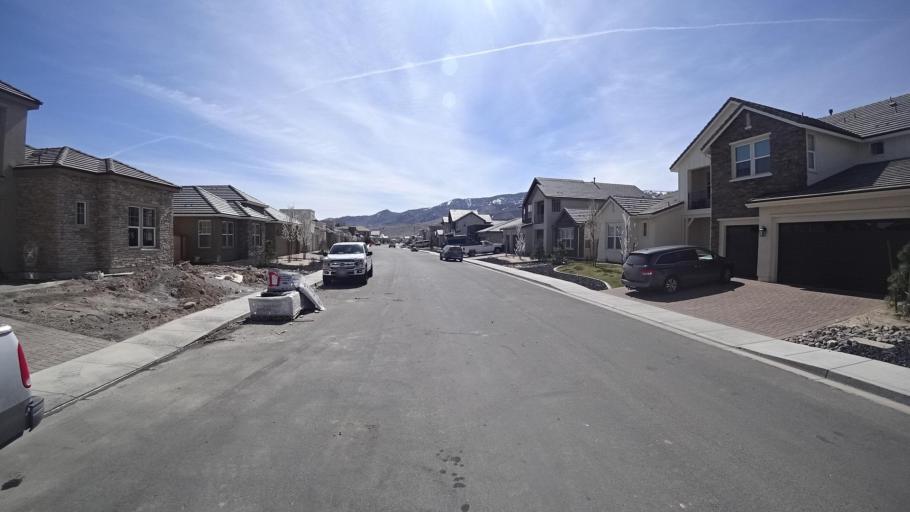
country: US
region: Nevada
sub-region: Washoe County
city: Verdi
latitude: 39.5185
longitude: -119.9792
